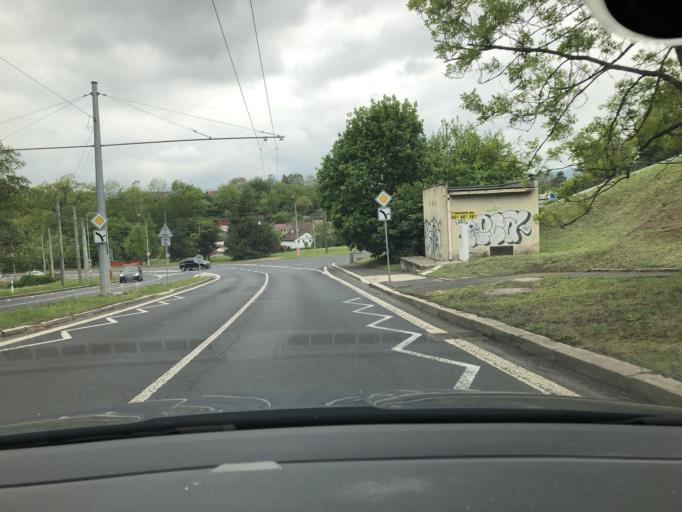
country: CZ
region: Ustecky
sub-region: Okres Usti nad Labem
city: Usti nad Labem
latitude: 50.6834
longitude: 14.0181
